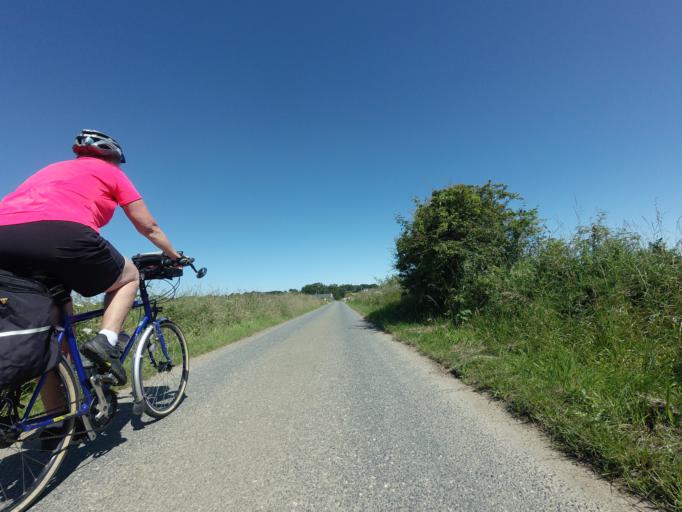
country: GB
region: Scotland
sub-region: Aberdeenshire
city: Macduff
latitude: 57.6299
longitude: -2.4850
